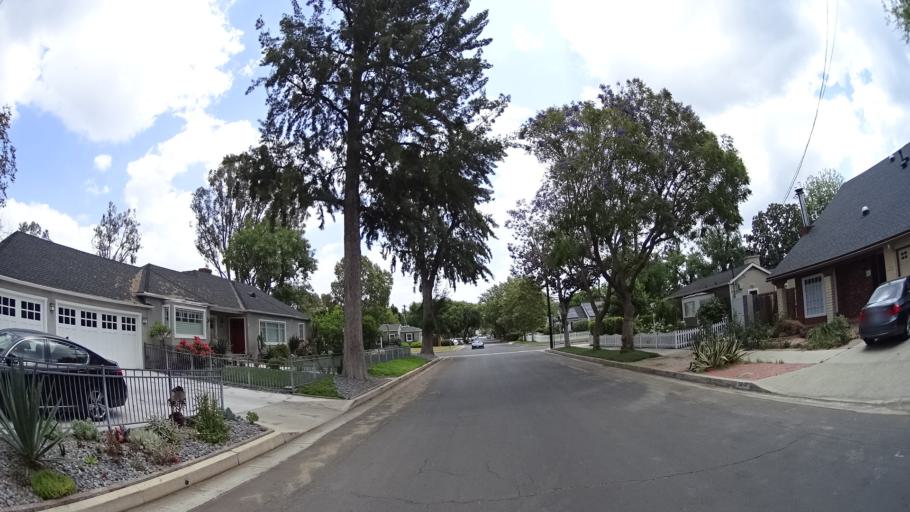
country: US
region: California
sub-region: Los Angeles County
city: Sherman Oaks
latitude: 34.1540
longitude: -118.4177
